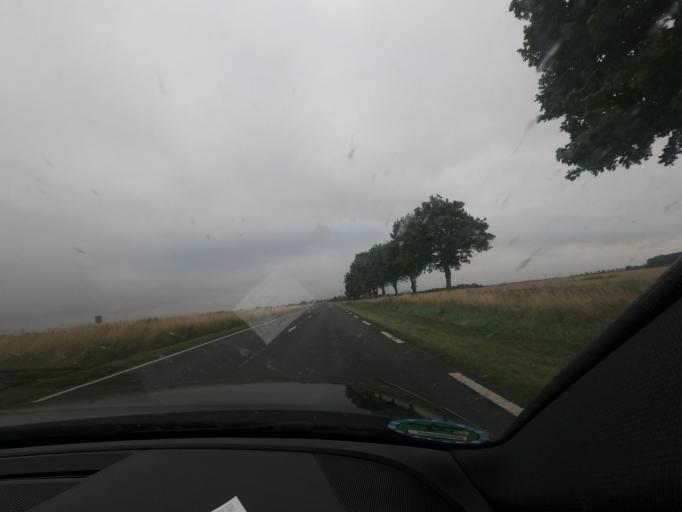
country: FR
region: Picardie
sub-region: Departement de la Somme
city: Rosieres-en-Santerre
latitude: 49.7567
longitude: 2.6484
